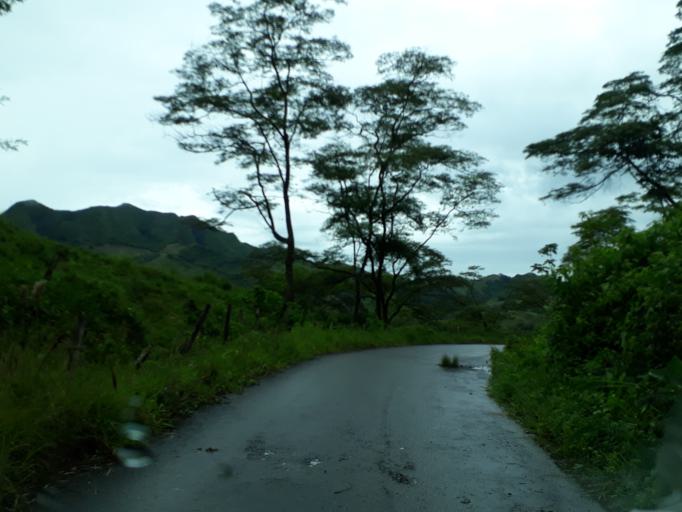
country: CO
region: Cundinamarca
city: Medina
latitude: 4.6789
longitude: -73.3191
